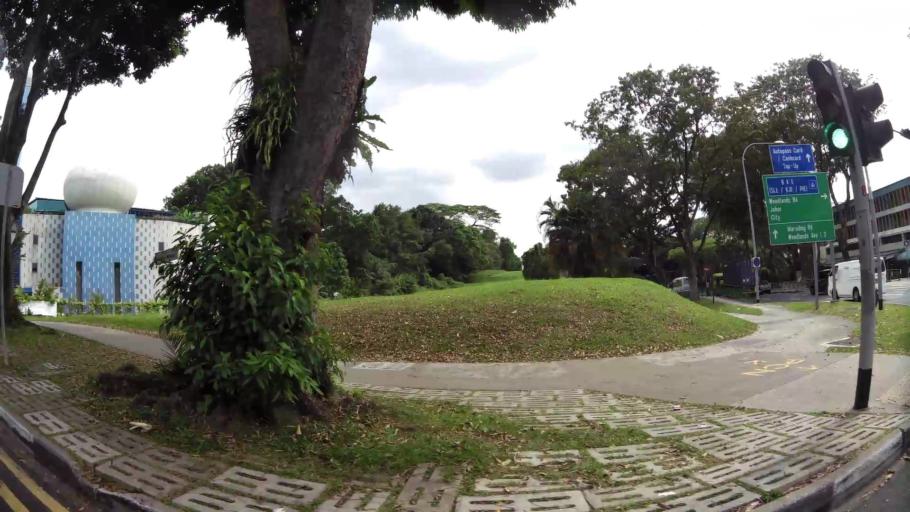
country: MY
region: Johor
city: Johor Bahru
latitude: 1.4410
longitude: 103.7711
